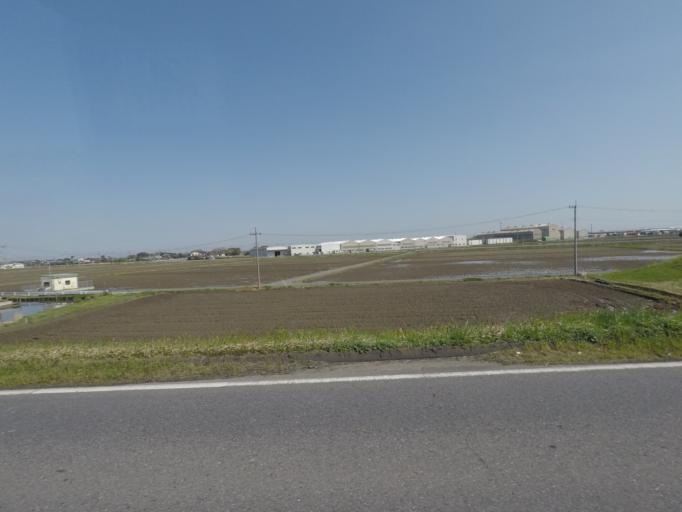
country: JP
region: Chiba
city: Katori-shi
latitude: 35.9194
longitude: 140.4692
